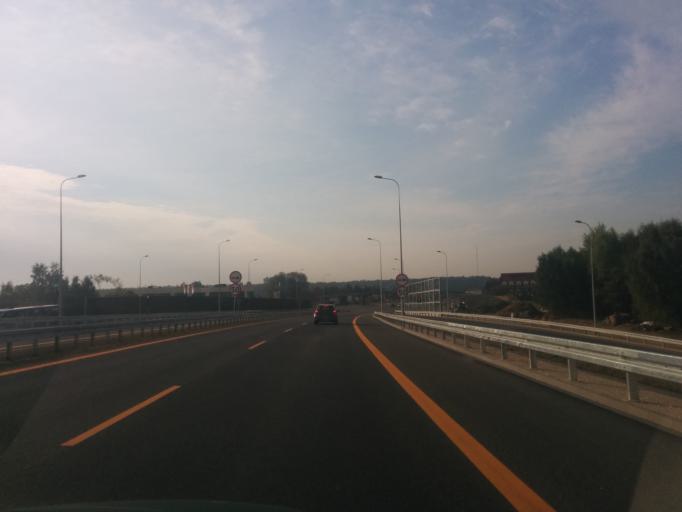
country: PL
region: Masovian Voivodeship
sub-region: Powiat pruszkowski
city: Nowe Grocholice
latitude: 52.1135
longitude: 20.8890
